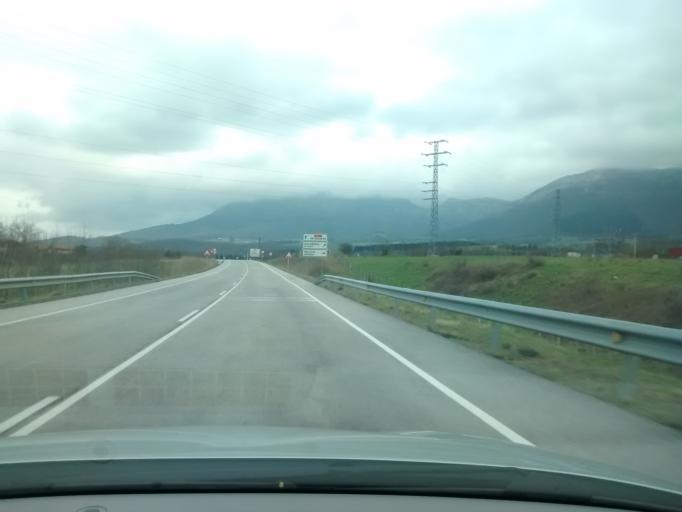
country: ES
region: Castille and Leon
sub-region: Provincia de Burgos
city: Villasana de Mena
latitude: 43.0941
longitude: -3.2947
